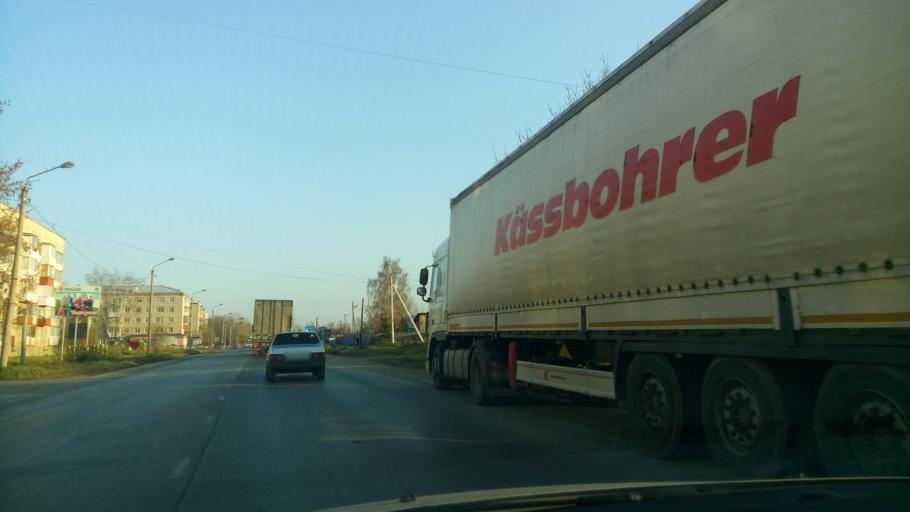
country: RU
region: Sverdlovsk
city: Bogdanovich
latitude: 56.7717
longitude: 62.0423
